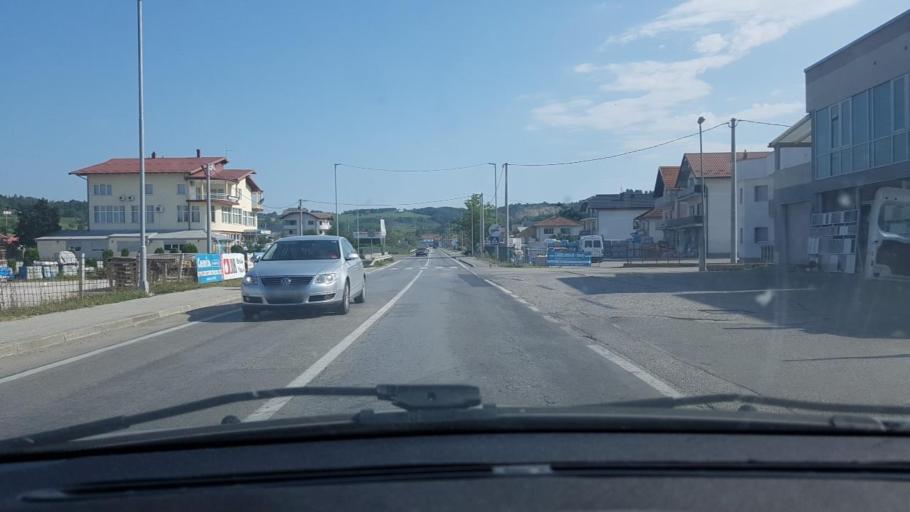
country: BA
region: Federation of Bosnia and Herzegovina
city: Coralici
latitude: 44.9851
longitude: 15.8945
